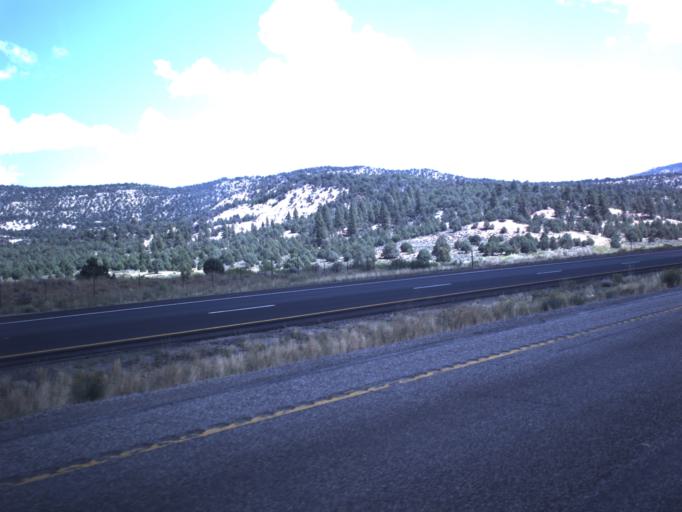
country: US
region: Utah
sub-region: Sevier County
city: Salina
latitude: 38.8818
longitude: -111.5742
